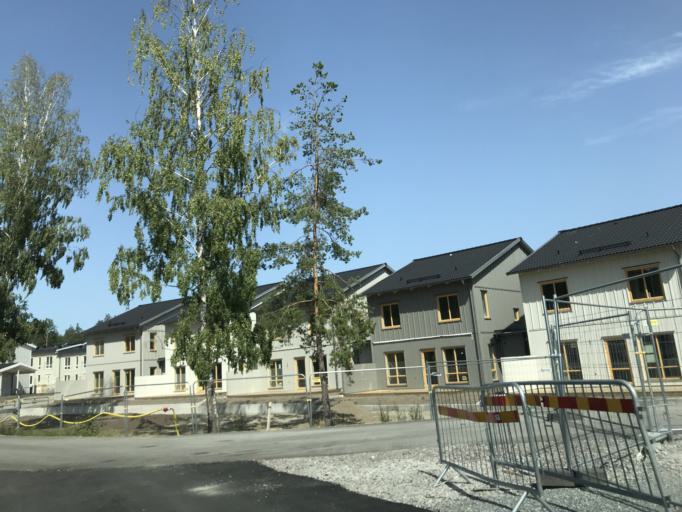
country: SE
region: Stockholm
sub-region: Solna Kommun
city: Rasunda
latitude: 59.3862
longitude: 17.9844
